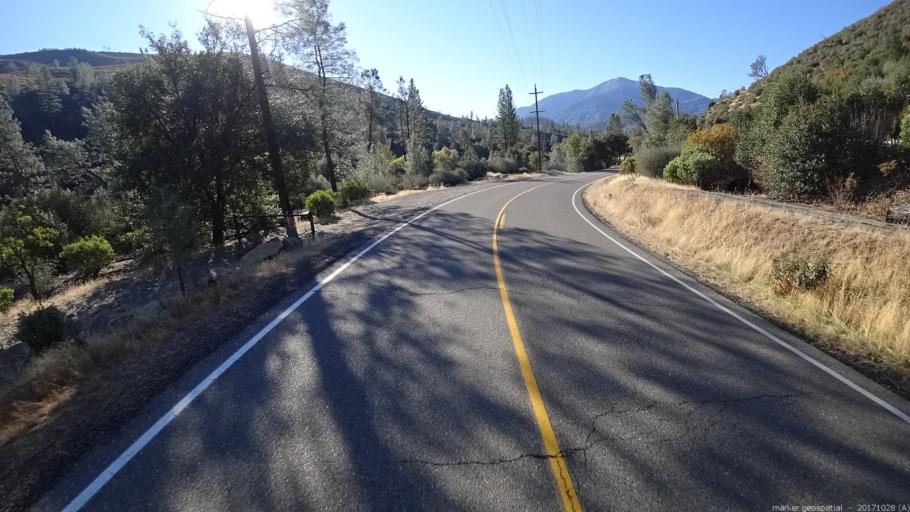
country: US
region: California
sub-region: Shasta County
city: Shasta
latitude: 40.6786
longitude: -122.6346
